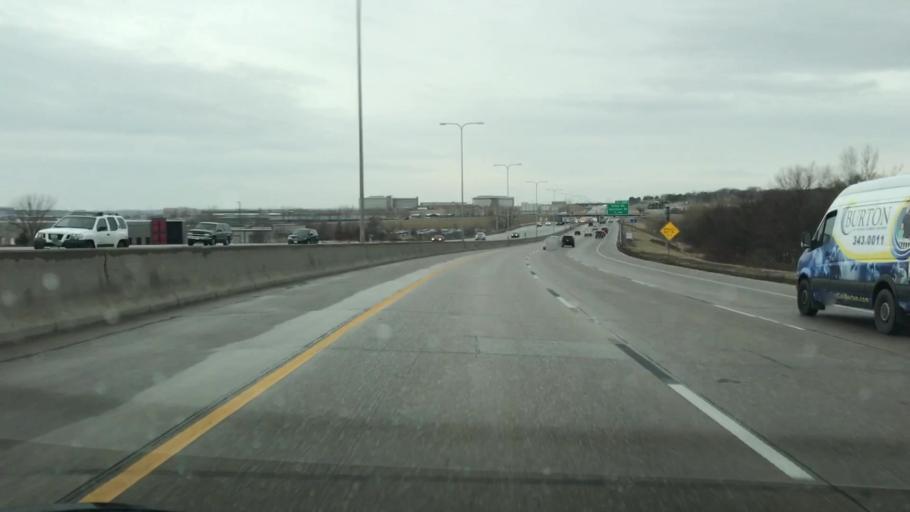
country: US
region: Nebraska
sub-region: Sarpy County
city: Chalco
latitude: 41.1931
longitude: -96.0979
